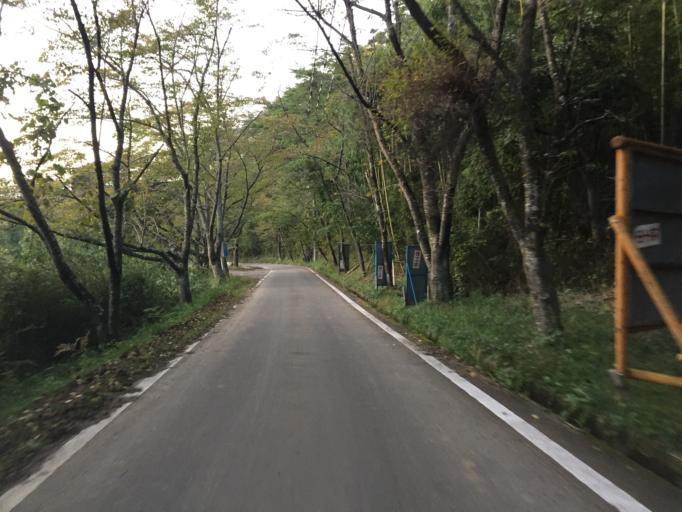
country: JP
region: Fukushima
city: Yanagawamachi-saiwaicho
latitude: 37.8521
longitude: 140.6313
